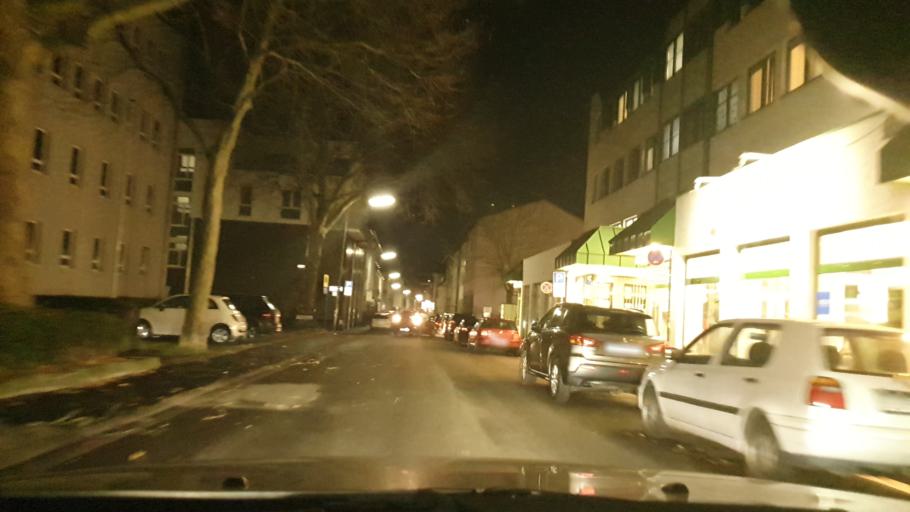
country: DE
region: Rheinland-Pfalz
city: Kaiserslautern
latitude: 49.4391
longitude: 7.7732
